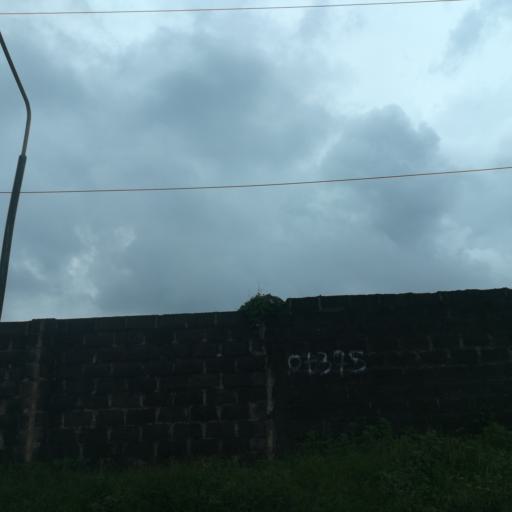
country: NG
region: Rivers
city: Port Harcourt
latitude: 4.8249
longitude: 7.0370
